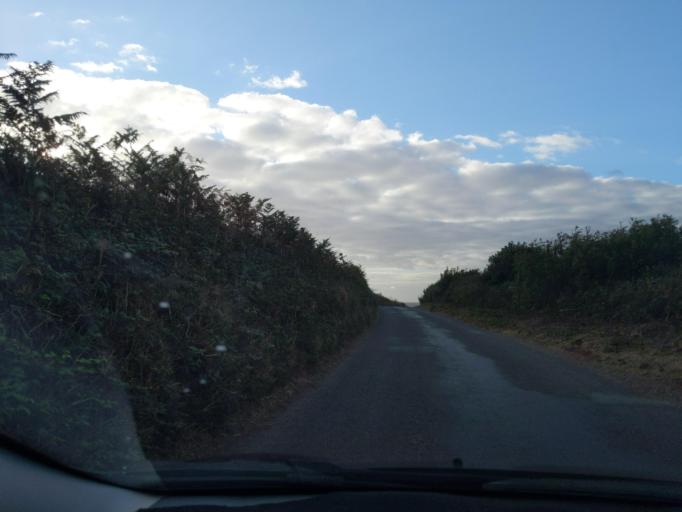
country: GB
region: England
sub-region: Devon
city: Salcombe
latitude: 50.2321
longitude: -3.8154
